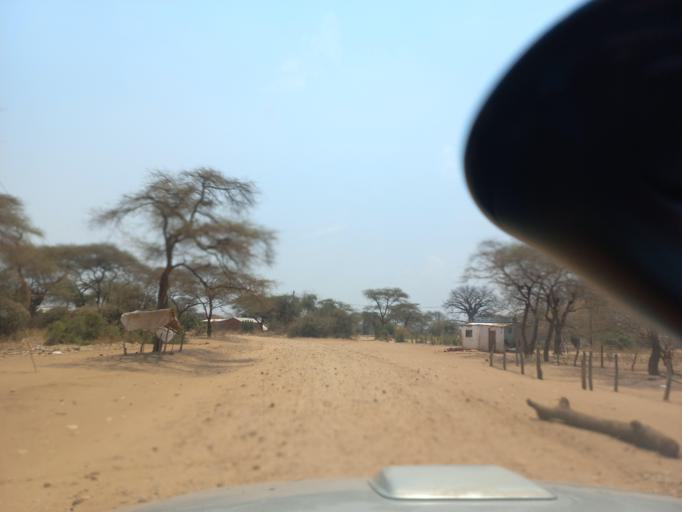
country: ZW
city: Chirundu
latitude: -15.9420
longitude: 28.8373
